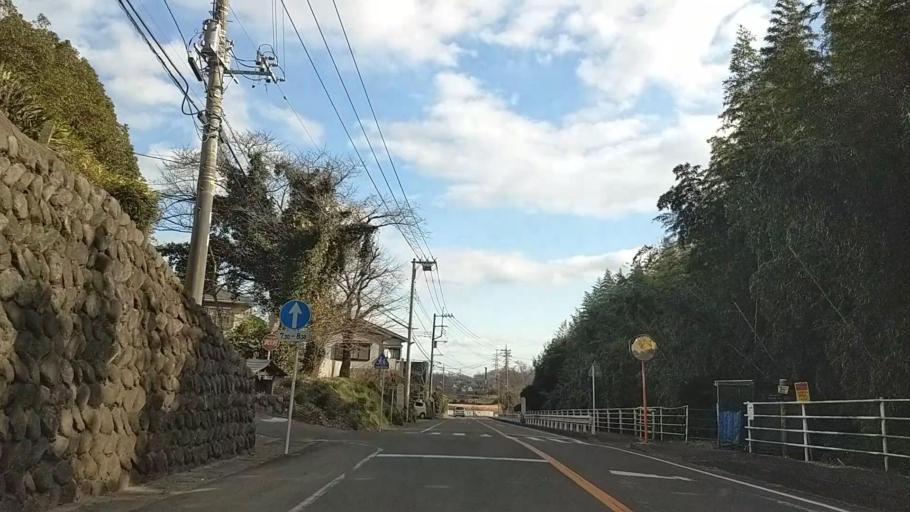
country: JP
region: Kanagawa
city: Isehara
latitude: 35.4205
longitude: 139.2907
